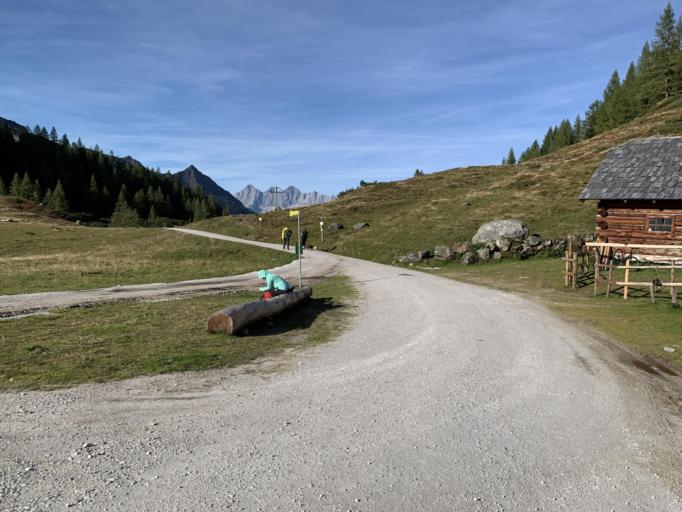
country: AT
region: Salzburg
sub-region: Politischer Bezirk Sankt Johann im Pongau
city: Forstau
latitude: 47.2967
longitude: 13.6239
